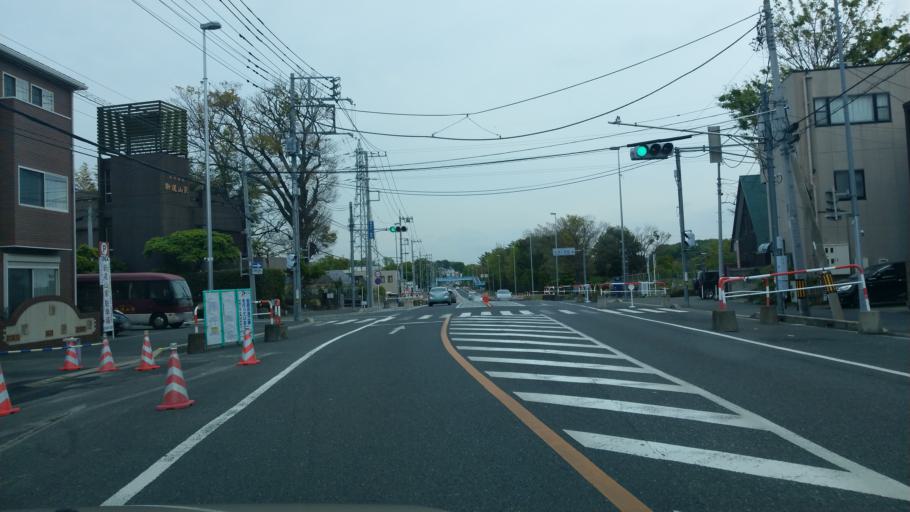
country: JP
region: Saitama
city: Saitama
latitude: 35.9141
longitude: 139.6388
